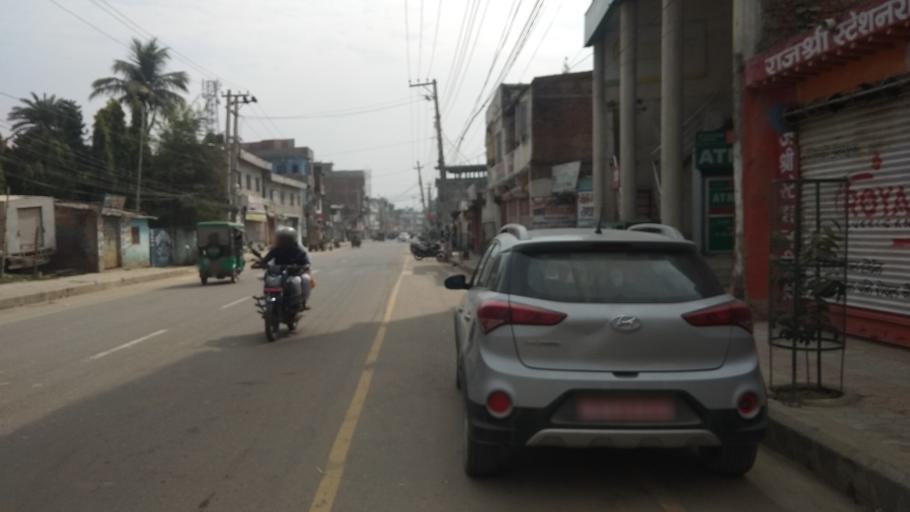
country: NP
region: Central Region
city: Janakpur
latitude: 26.7338
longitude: 85.9326
